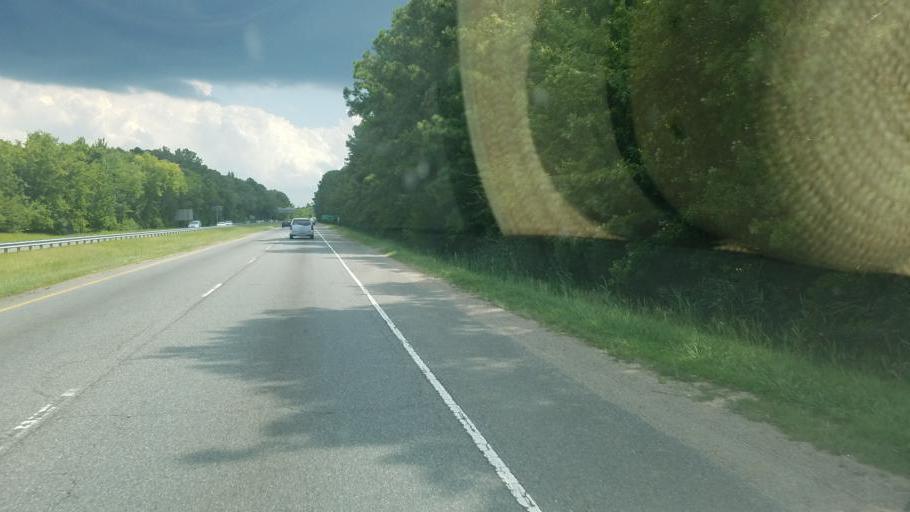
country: US
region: Virginia
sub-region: City of Chesapeake
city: Chesapeake
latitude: 36.7316
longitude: -76.2334
